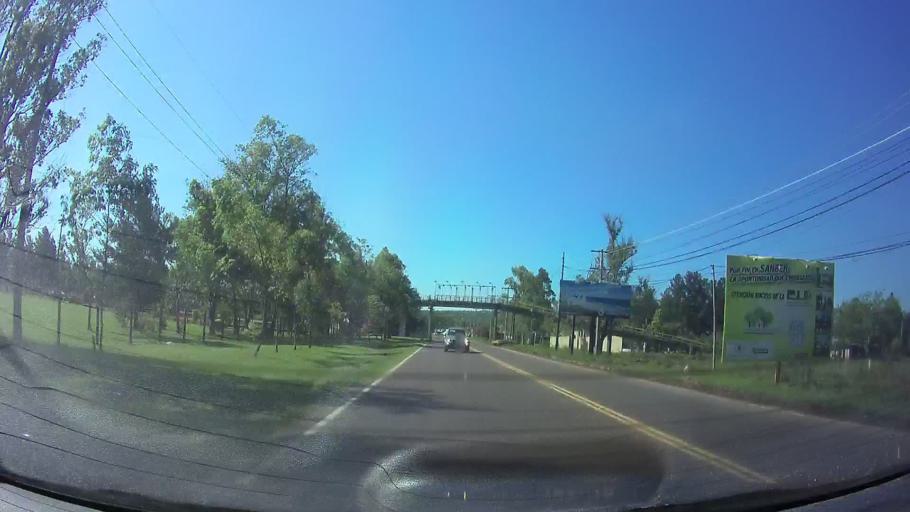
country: PY
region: Cordillera
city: San Bernardino
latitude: -25.3403
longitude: -57.2737
